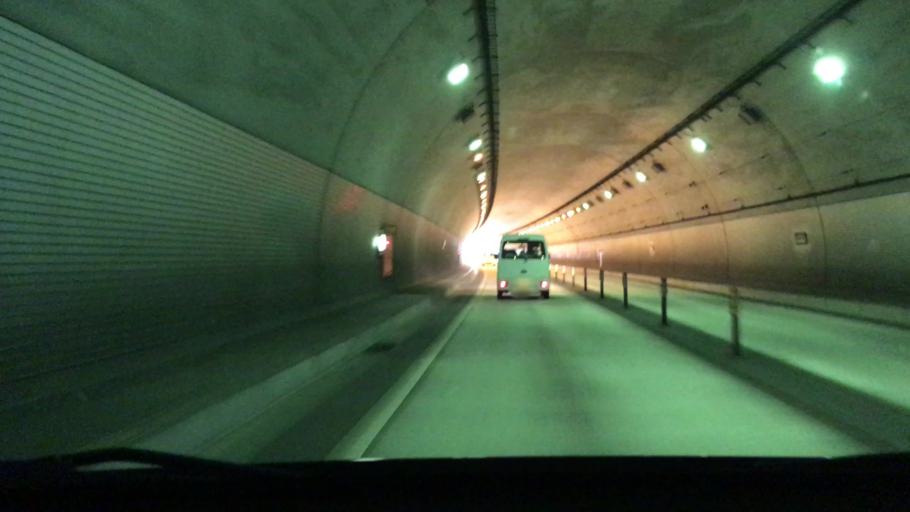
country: JP
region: Nagasaki
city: Sasebo
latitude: 33.0996
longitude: 129.7793
